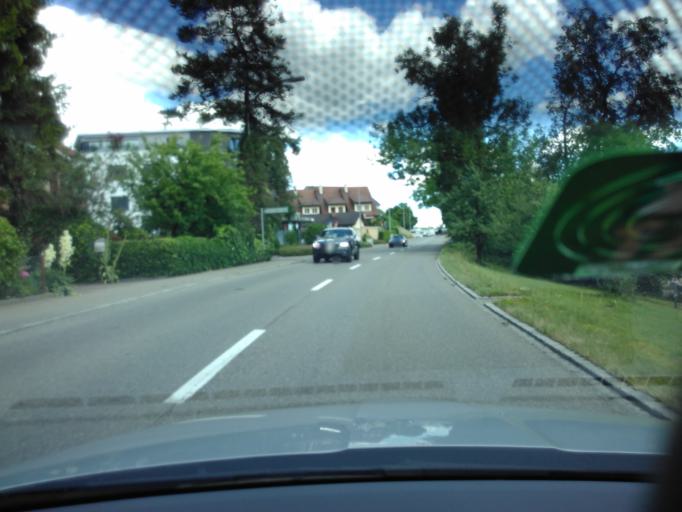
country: CH
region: Aargau
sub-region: Bezirk Muri
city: Oberruti
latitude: 47.1493
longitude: 8.3940
